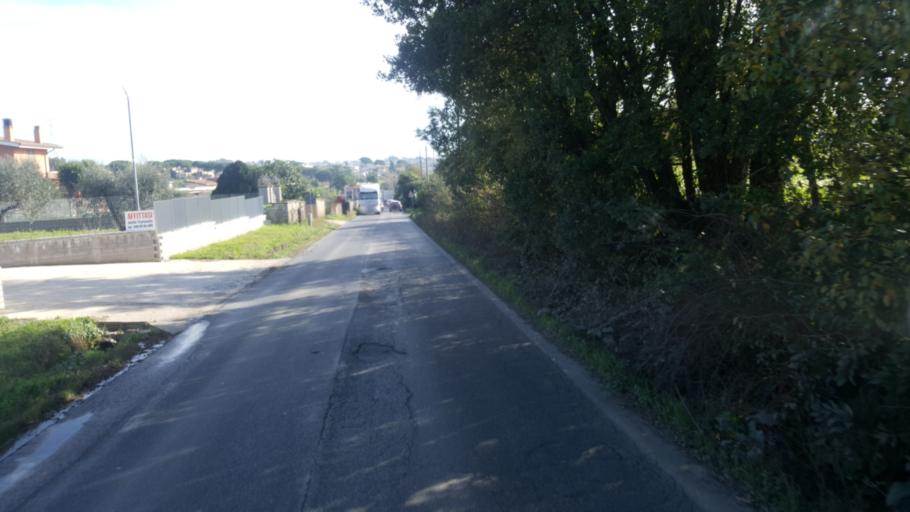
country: IT
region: Latium
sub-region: Citta metropolitana di Roma Capitale
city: Mantiglia di Ardea
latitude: 41.6807
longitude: 12.6203
